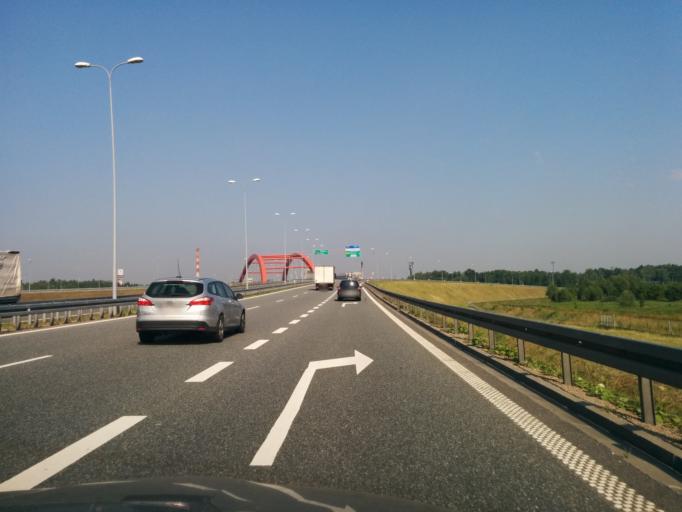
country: PL
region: Silesian Voivodeship
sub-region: Powiat gliwicki
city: Przyszowice
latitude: 50.2676
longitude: 18.7335
